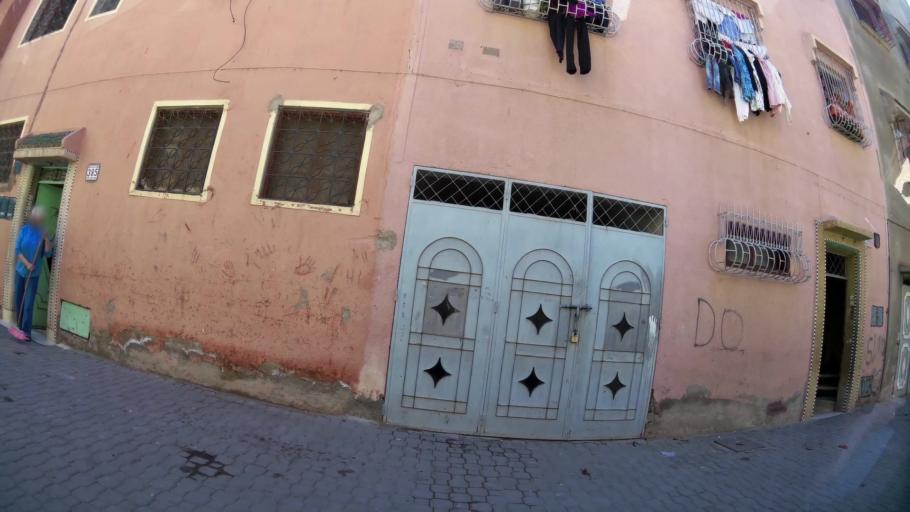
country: MA
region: Marrakech-Tensift-Al Haouz
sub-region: Marrakech
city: Marrakesh
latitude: 31.6355
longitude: -8.0663
